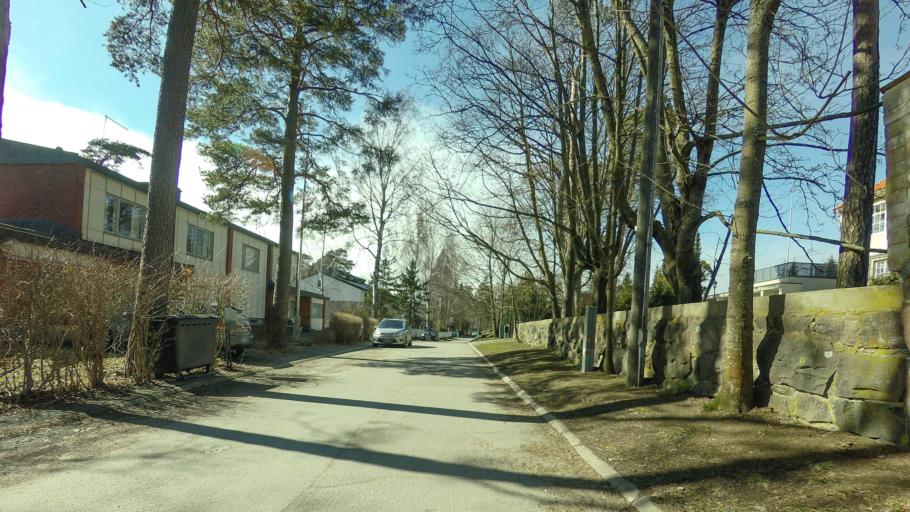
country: FI
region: Uusimaa
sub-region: Helsinki
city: Helsinki
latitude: 60.1803
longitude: 25.0130
